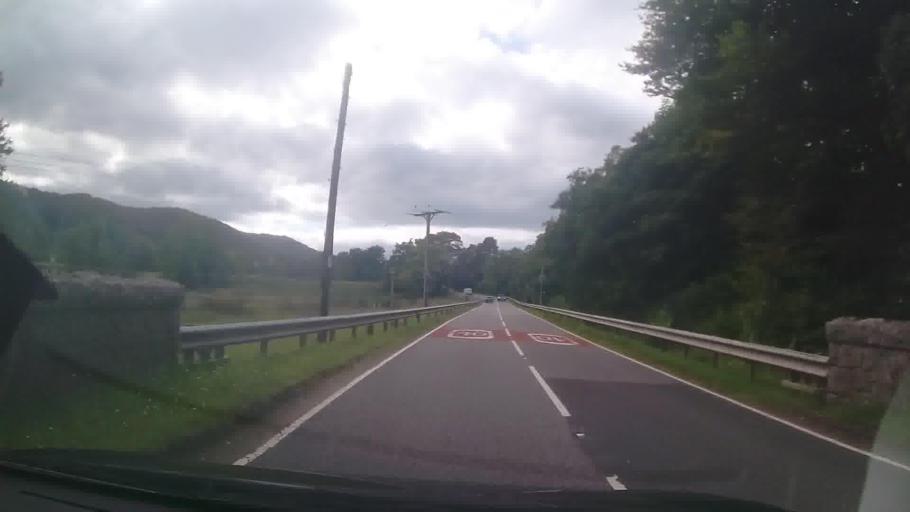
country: GB
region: Scotland
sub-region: Highland
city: Fort William
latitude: 56.6415
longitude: -5.2828
